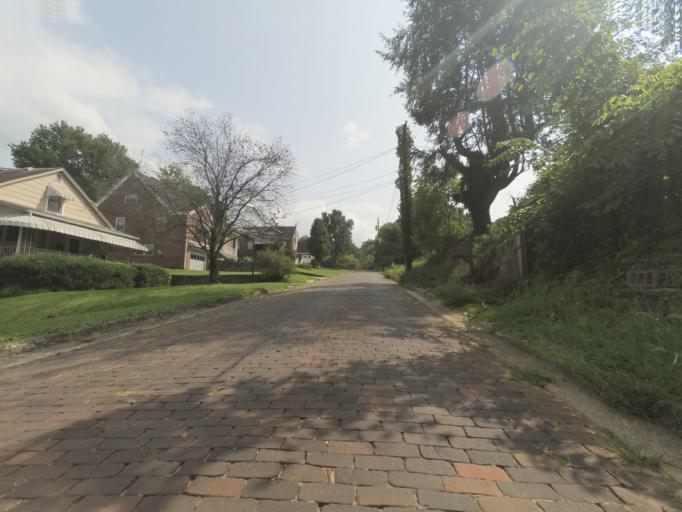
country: US
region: West Virginia
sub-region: Cabell County
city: Huntington
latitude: 38.4013
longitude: -82.4041
